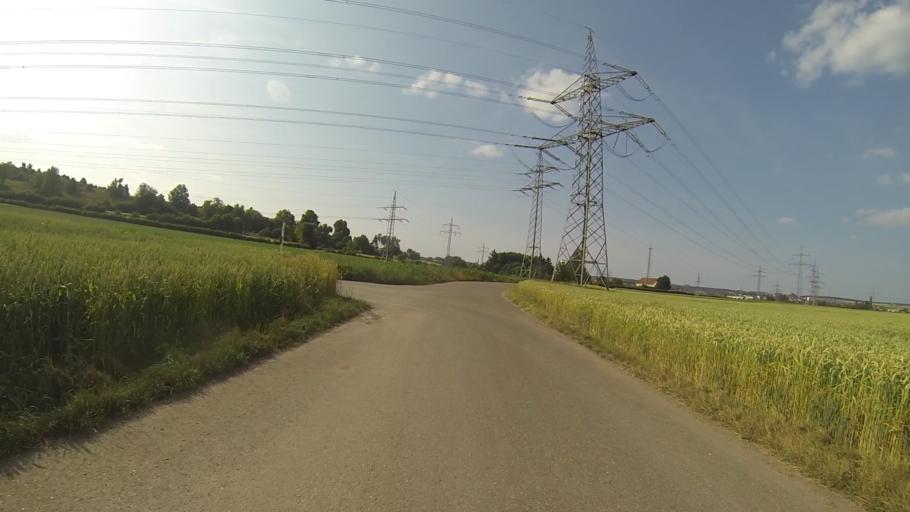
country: DE
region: Baden-Wuerttemberg
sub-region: Regierungsbezirk Stuttgart
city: Niederstotzingen
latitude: 48.5237
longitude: 10.2303
